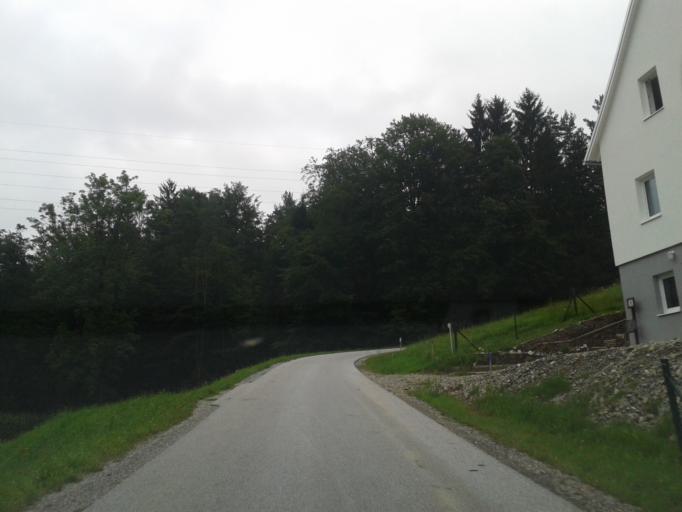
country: AT
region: Styria
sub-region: Politischer Bezirk Weiz
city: Sankt Ruprecht an der Raab
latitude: 47.1188
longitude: 15.6369
